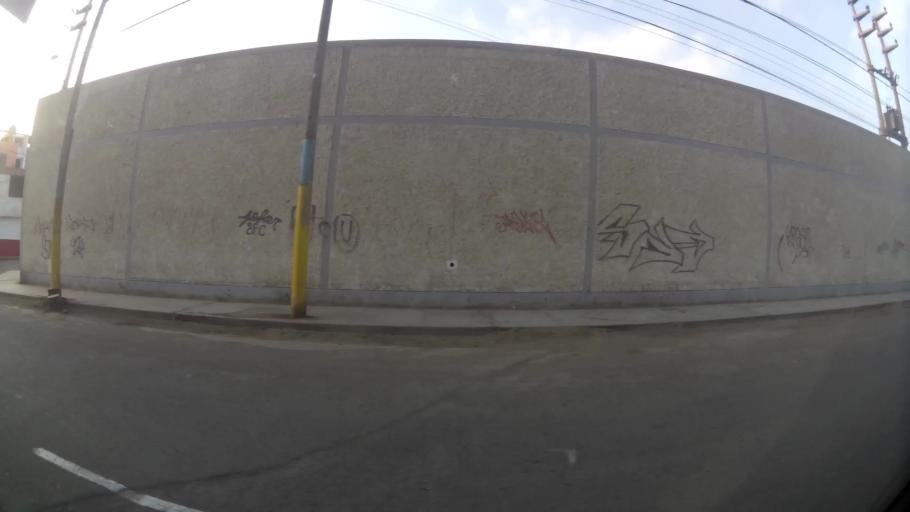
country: PE
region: Lima
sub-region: Huaura
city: Huacho
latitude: -11.1083
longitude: -77.5986
